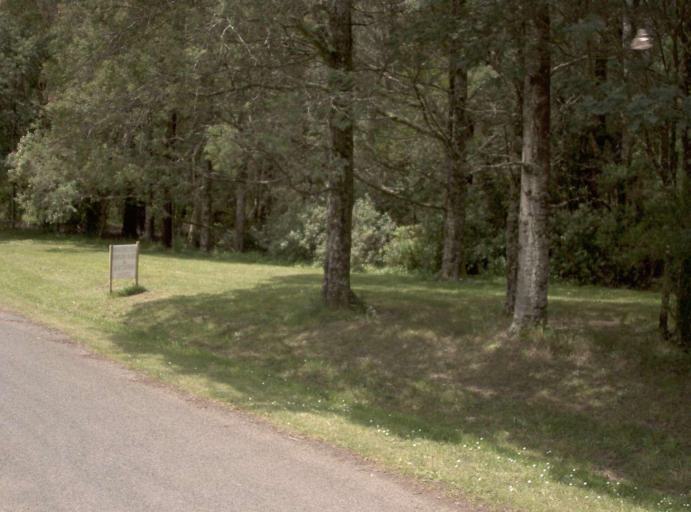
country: AU
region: Victoria
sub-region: Latrobe
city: Traralgon
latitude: -38.4281
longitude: 146.5660
